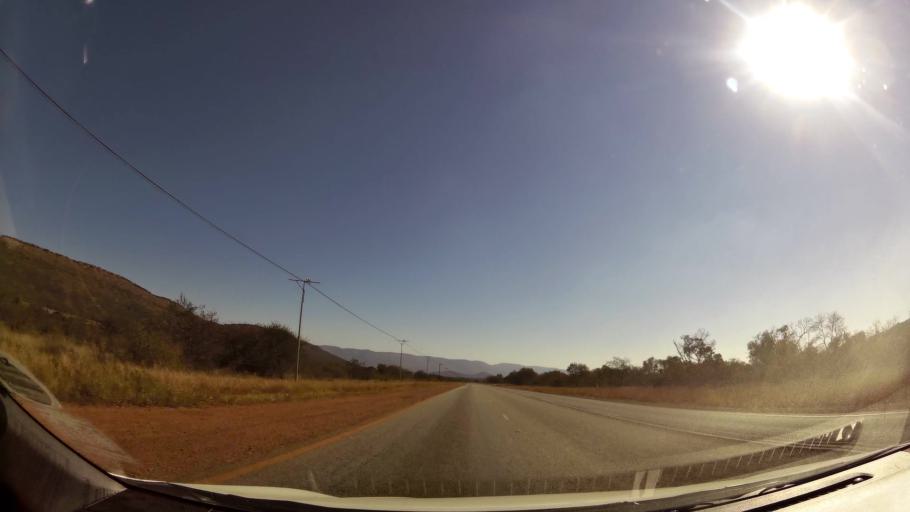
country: ZA
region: Limpopo
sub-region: Waterberg District Municipality
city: Mokopane
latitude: -24.1636
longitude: 29.0640
